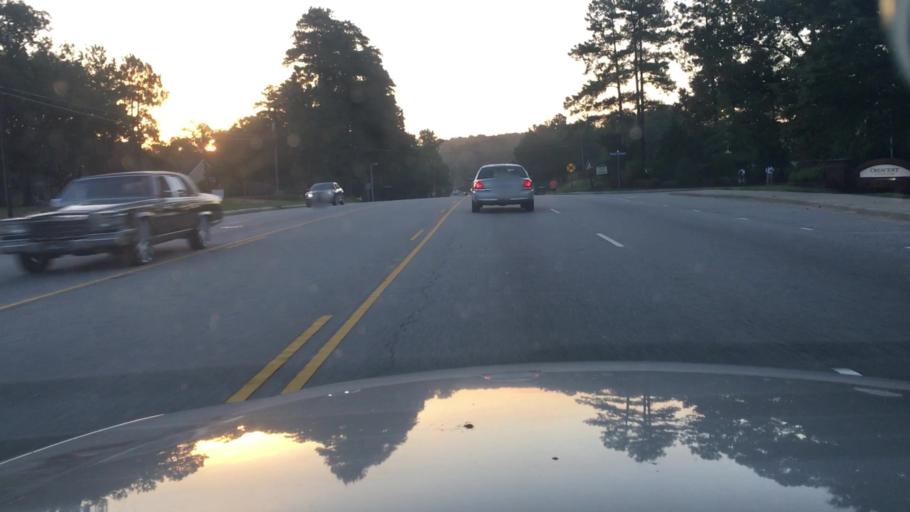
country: US
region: North Carolina
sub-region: Cumberland County
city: Fort Bragg
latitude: 35.0587
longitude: -78.9860
